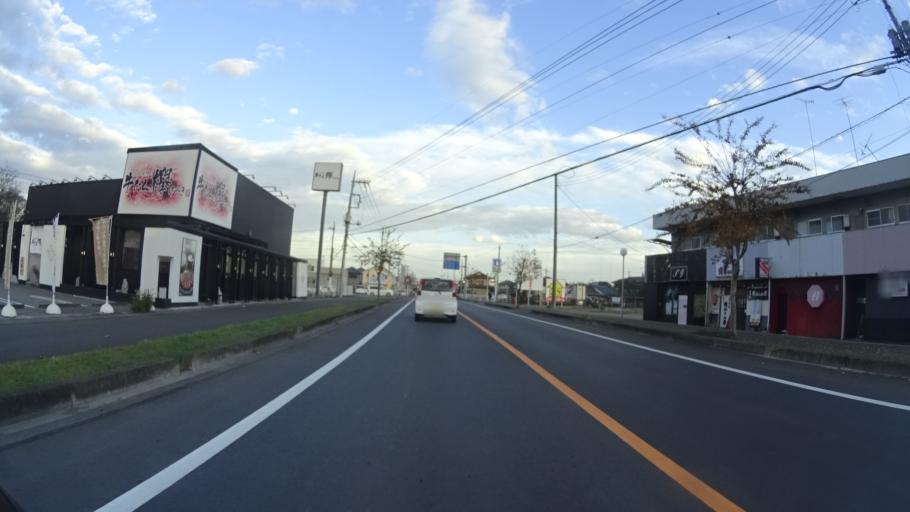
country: JP
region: Tochigi
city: Tochigi
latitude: 36.3920
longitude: 139.7271
